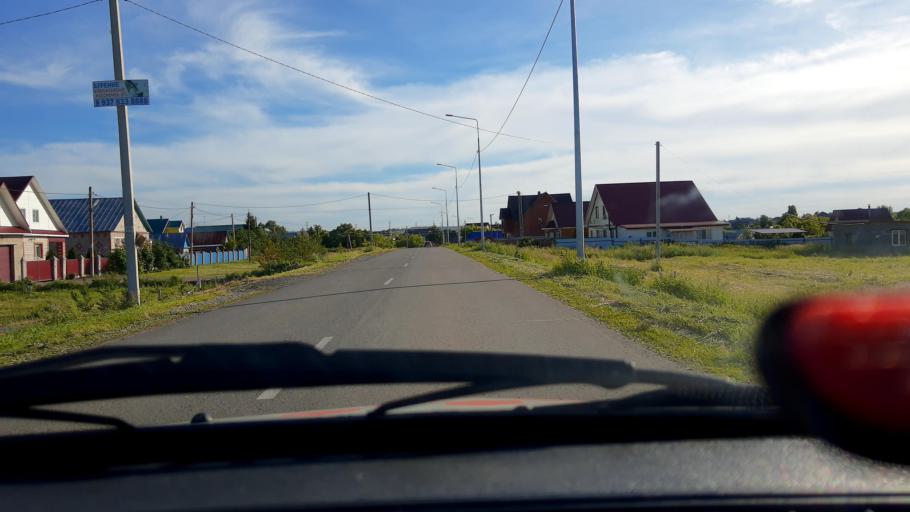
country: RU
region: Bashkortostan
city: Kabakovo
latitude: 54.5046
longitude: 55.9259
